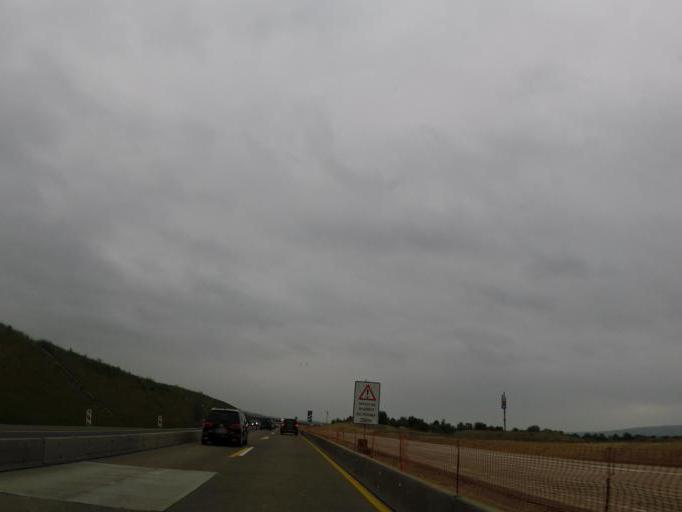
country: DE
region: Lower Saxony
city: Bockenem
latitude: 51.9514
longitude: 10.1414
